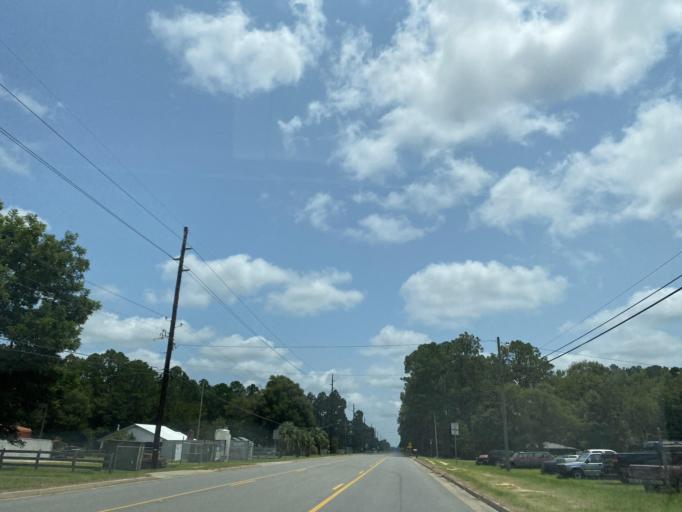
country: US
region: Georgia
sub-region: Jeff Davis County
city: Hazlehurst
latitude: 31.8454
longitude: -82.5869
